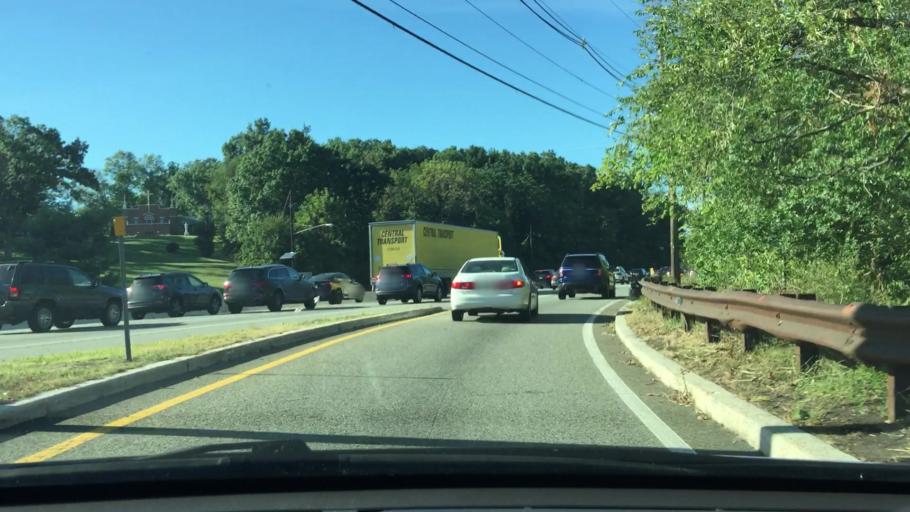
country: US
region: New Jersey
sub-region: Passaic County
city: Clifton
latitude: 40.8578
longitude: -74.1795
